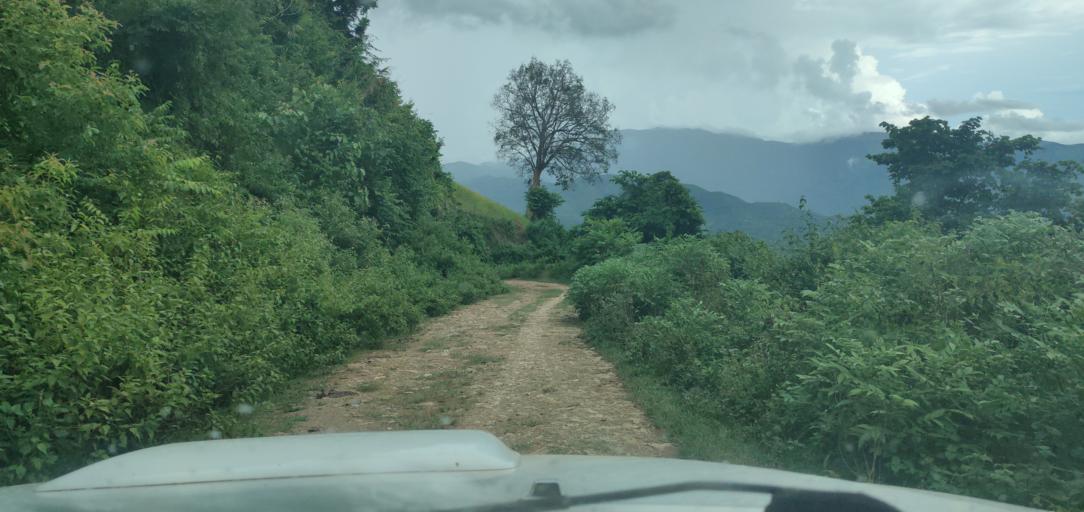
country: LA
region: Phongsali
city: Phongsali
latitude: 21.4416
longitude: 102.3192
